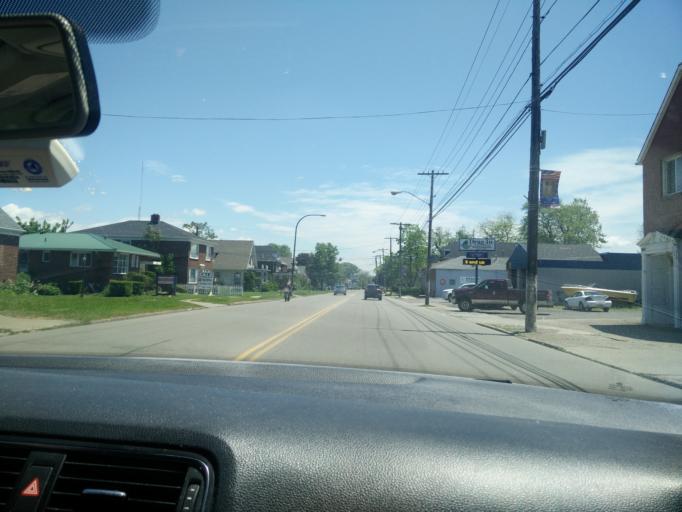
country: US
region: New York
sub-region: Erie County
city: Lackawanna
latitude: 42.8285
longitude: -78.8083
